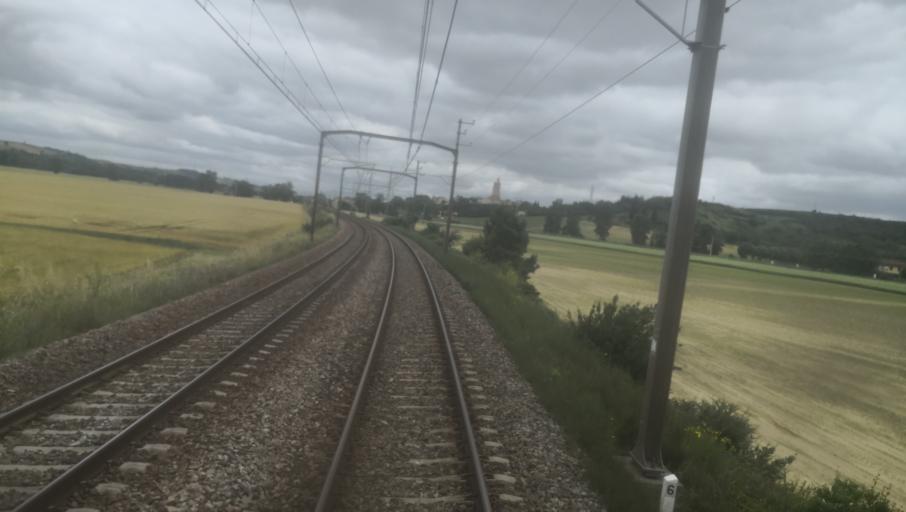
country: FR
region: Midi-Pyrenees
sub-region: Departement de la Haute-Garonne
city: Avignonet-Lauragais
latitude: 43.3603
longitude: 1.8011
